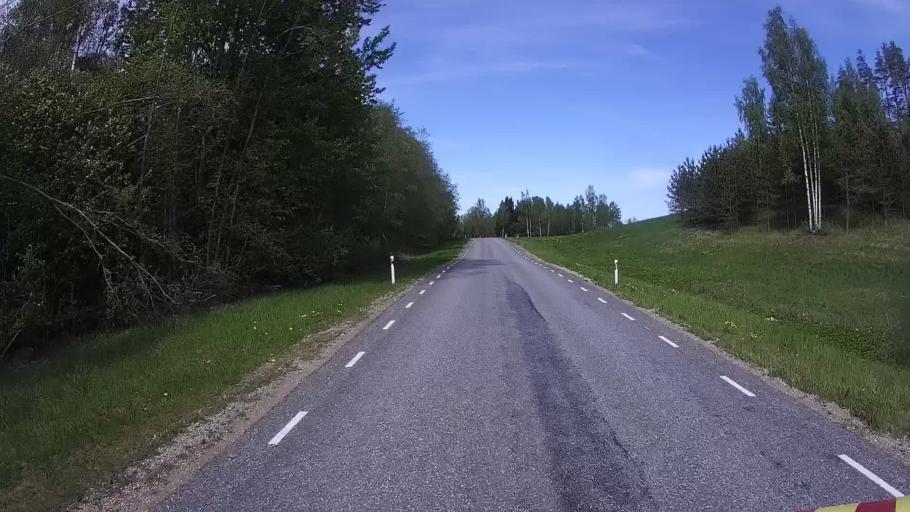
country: EE
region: Valgamaa
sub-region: Valga linn
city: Valga
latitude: 57.6751
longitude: 26.2834
